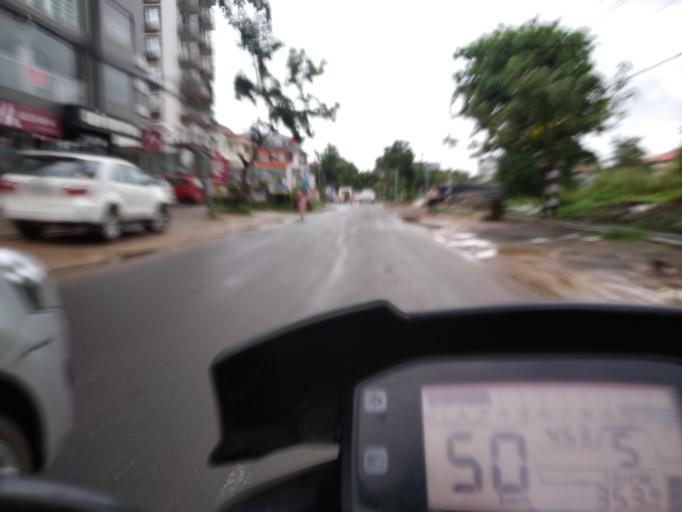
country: IN
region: Kerala
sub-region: Ernakulam
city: Cochin
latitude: 9.9729
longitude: 76.3074
